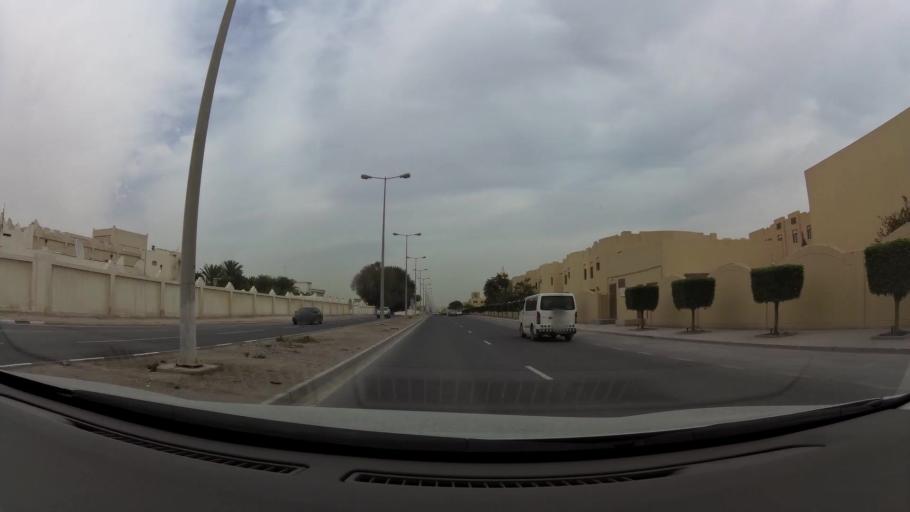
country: QA
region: Baladiyat ar Rayyan
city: Ar Rayyan
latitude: 25.2325
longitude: 51.4659
